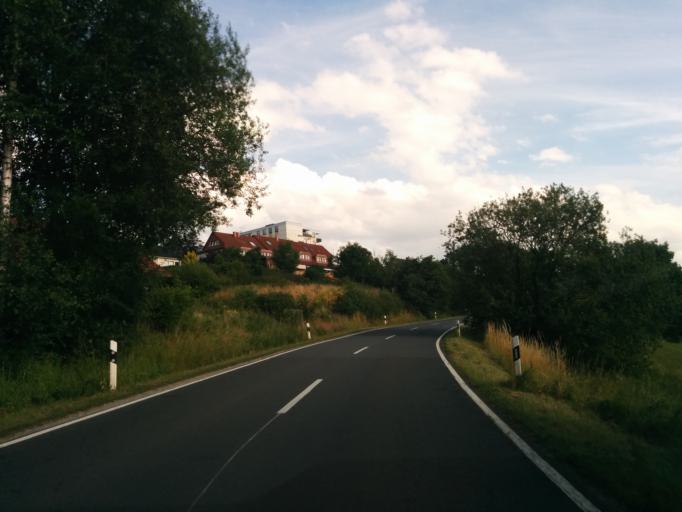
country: DE
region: Lower Saxony
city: Bad Lauterberg im Harz
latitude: 51.6193
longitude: 10.4650
